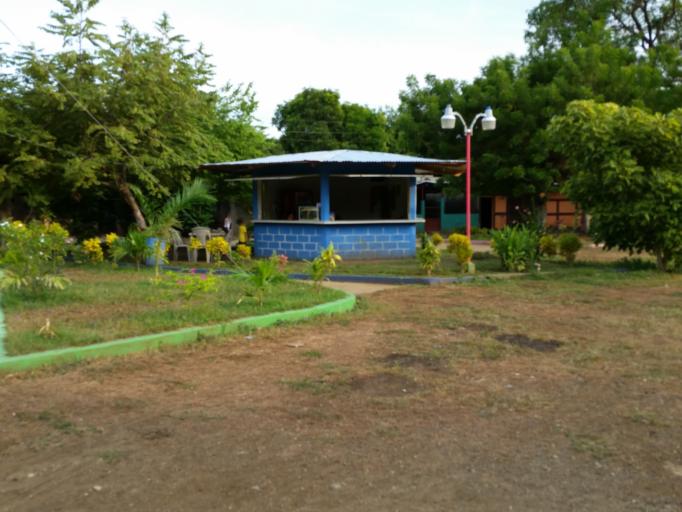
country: NI
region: Managua
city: Masachapa
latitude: 11.7883
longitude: -86.5143
